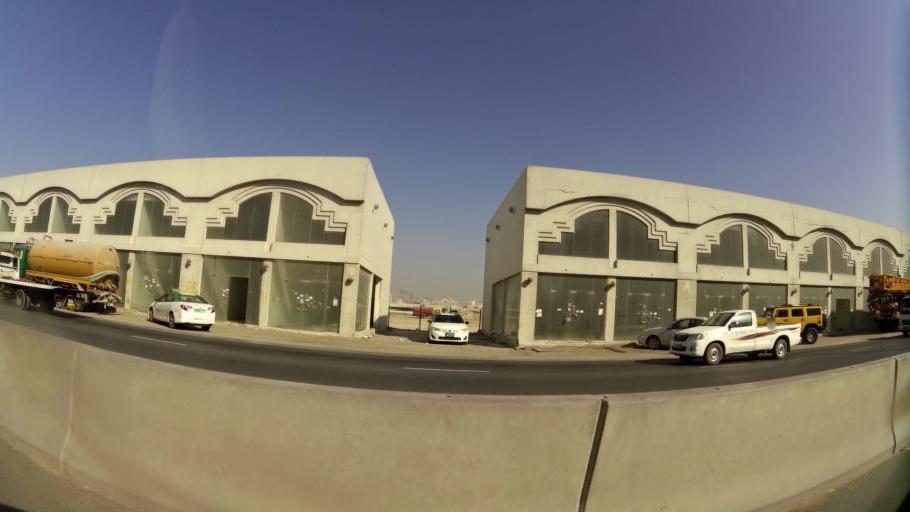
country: AE
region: Ash Shariqah
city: Sharjah
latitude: 25.3213
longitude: 55.4152
